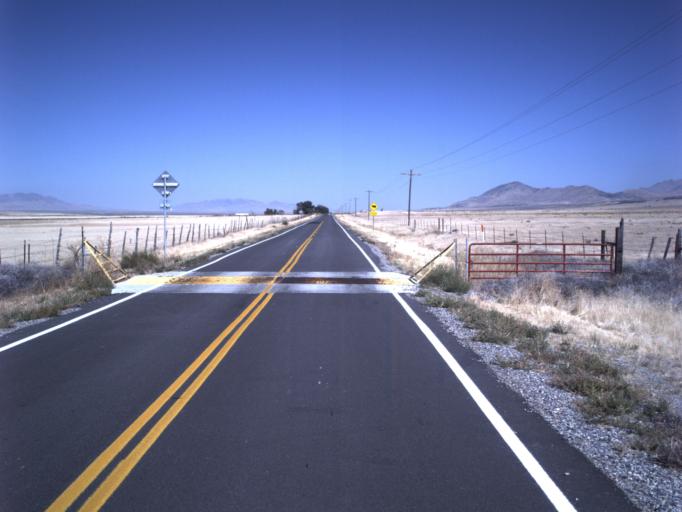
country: US
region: Utah
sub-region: Tooele County
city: Grantsville
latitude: 40.4181
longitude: -112.7488
